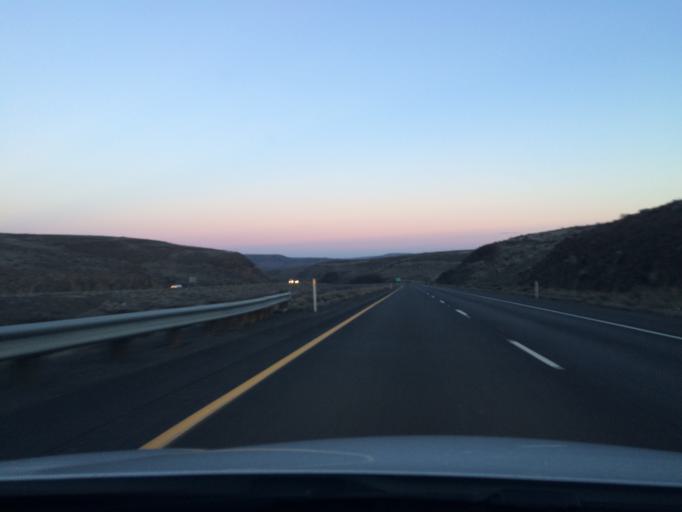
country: US
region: Washington
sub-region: Grant County
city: Mattawa
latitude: 46.9385
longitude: -120.0235
